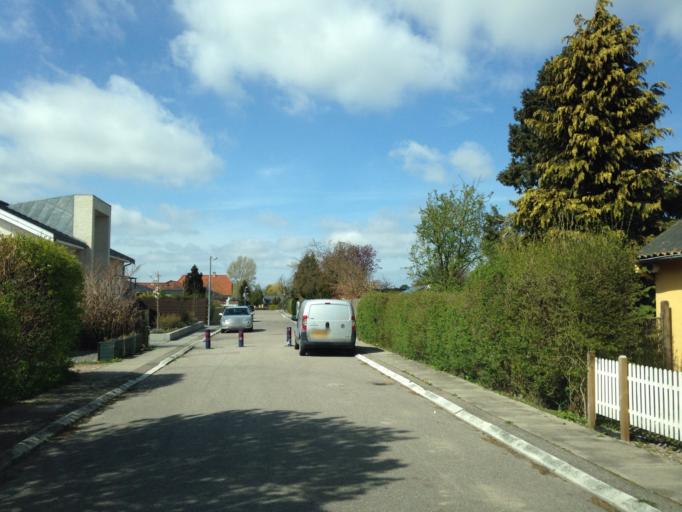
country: DK
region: Zealand
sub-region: Greve Kommune
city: Greve
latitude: 55.5826
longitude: 12.3099
